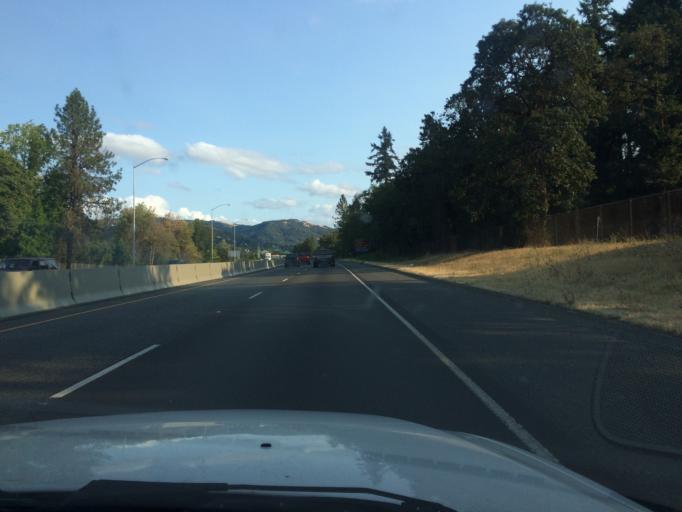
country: US
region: Oregon
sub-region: Douglas County
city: Roseburg
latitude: 43.2224
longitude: -123.3595
